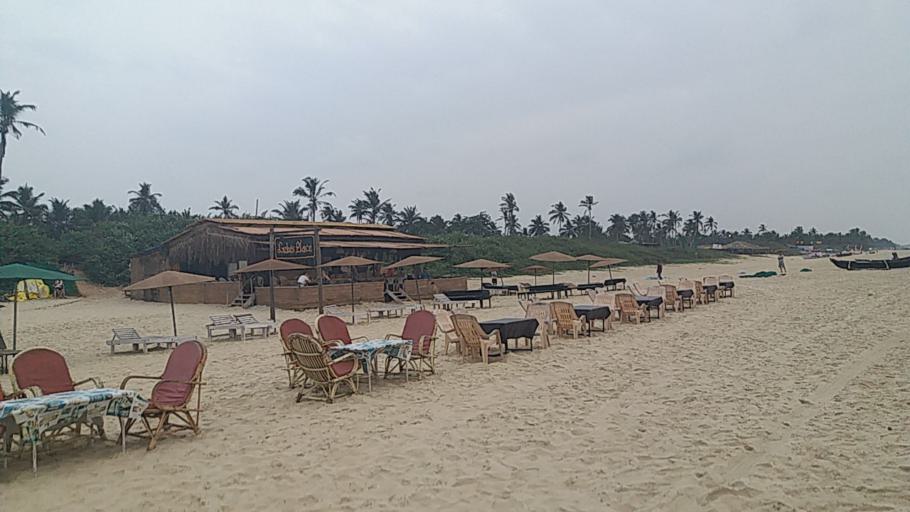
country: IN
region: Goa
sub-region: South Goa
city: Colva
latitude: 15.2748
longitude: 73.9136
